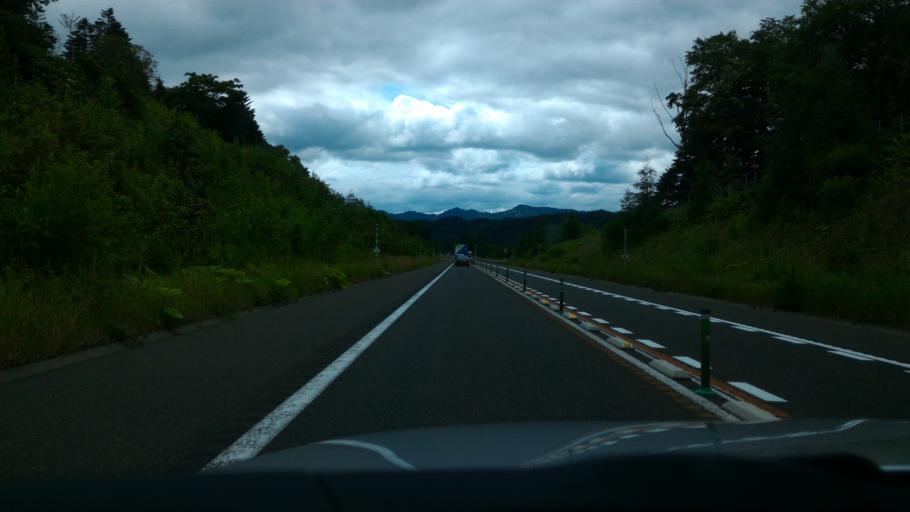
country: JP
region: Hokkaido
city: Shimo-furano
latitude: 42.9463
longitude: 142.2285
